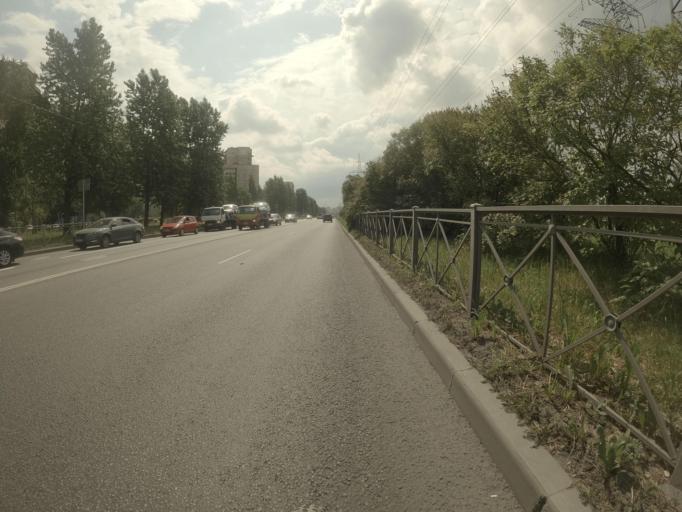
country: RU
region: St.-Petersburg
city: Krasnogvargeisky
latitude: 59.9537
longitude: 30.4608
